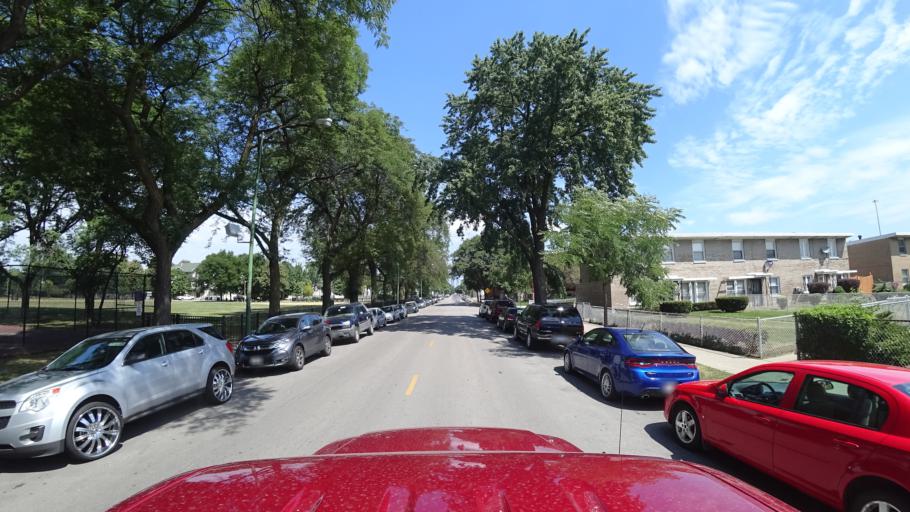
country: US
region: Illinois
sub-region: Cook County
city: Chicago
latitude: 41.8105
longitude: -87.6334
